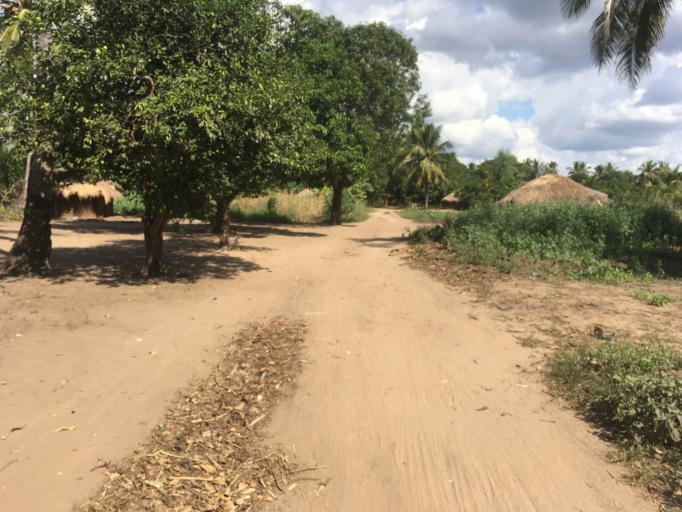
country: MZ
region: Zambezia
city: Quelimane
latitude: -17.6458
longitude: 36.6857
